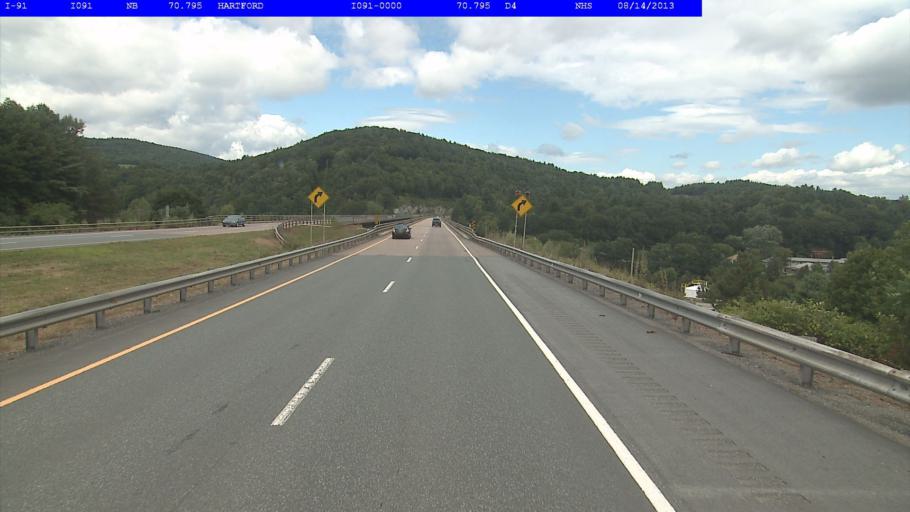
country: US
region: Vermont
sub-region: Windsor County
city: White River Junction
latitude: 43.6527
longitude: -72.3316
